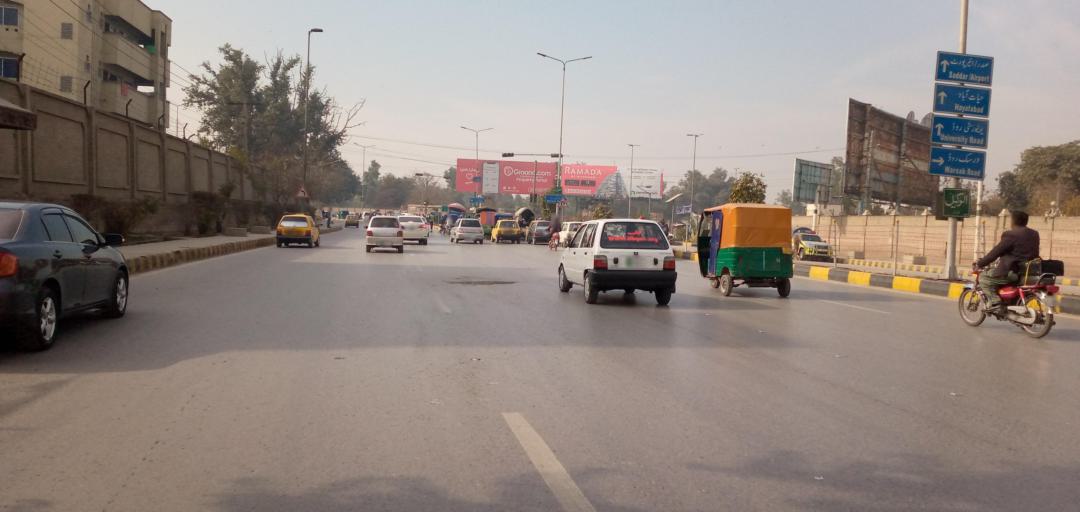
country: PK
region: Khyber Pakhtunkhwa
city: Peshawar
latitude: 34.0139
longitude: 71.5432
